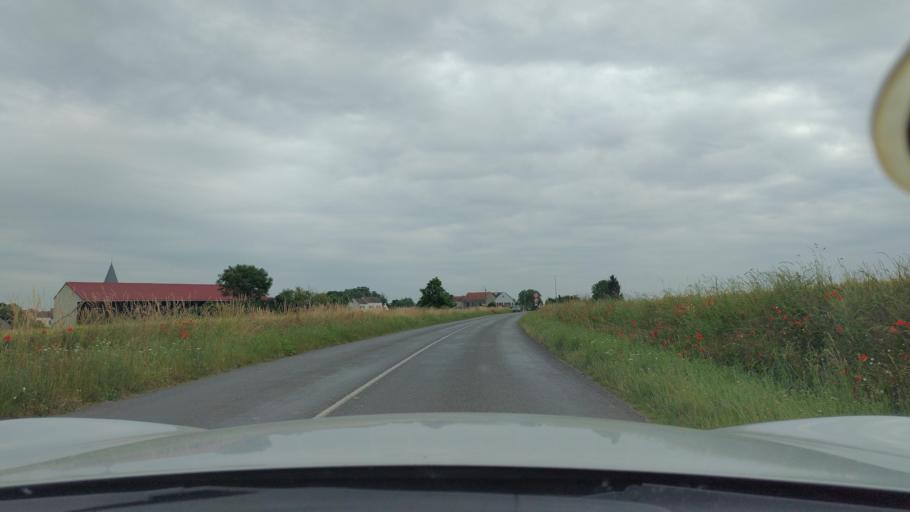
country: FR
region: Ile-de-France
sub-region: Departement de Seine-et-Marne
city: Cregy-les-Meaux
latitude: 49.0145
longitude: 2.8807
